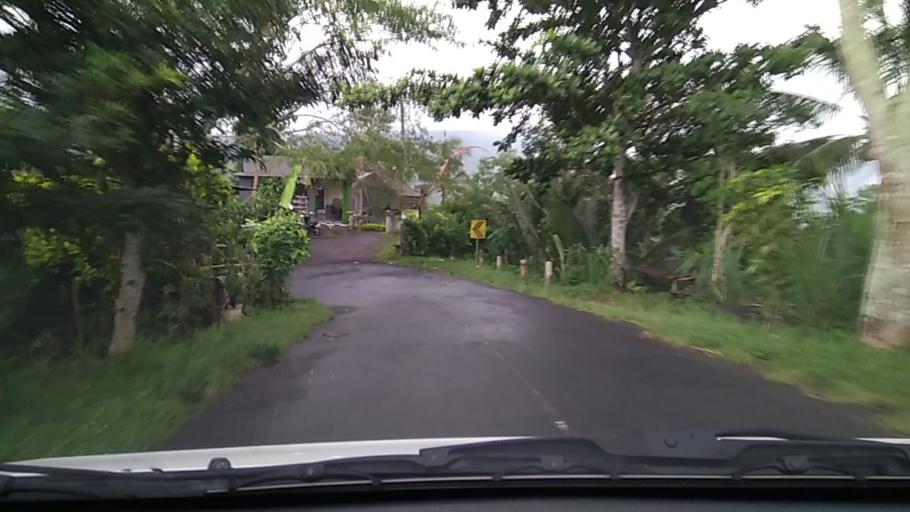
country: ID
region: Bali
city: Tistagede
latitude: -8.3915
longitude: 115.6252
